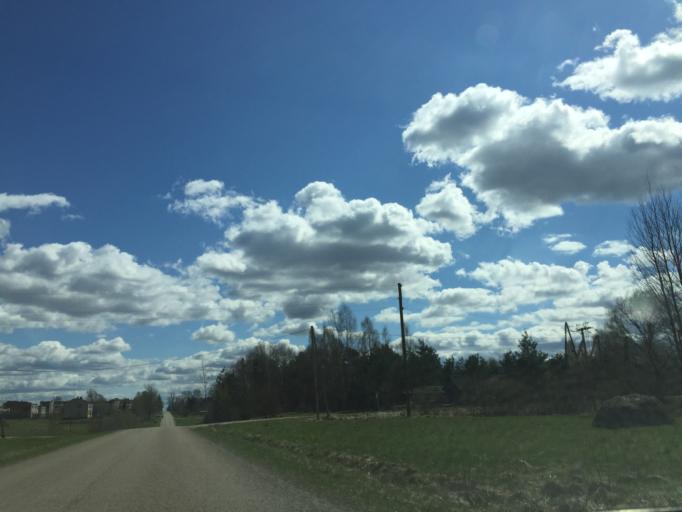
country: LV
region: Rezekne
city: Rezekne
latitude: 56.5697
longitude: 27.1375
